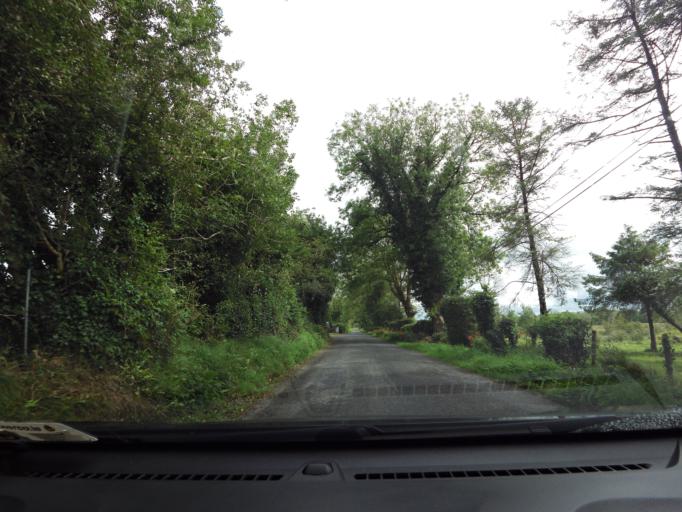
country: IE
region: Connaught
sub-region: County Galway
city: Loughrea
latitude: 53.3034
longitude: -8.6122
